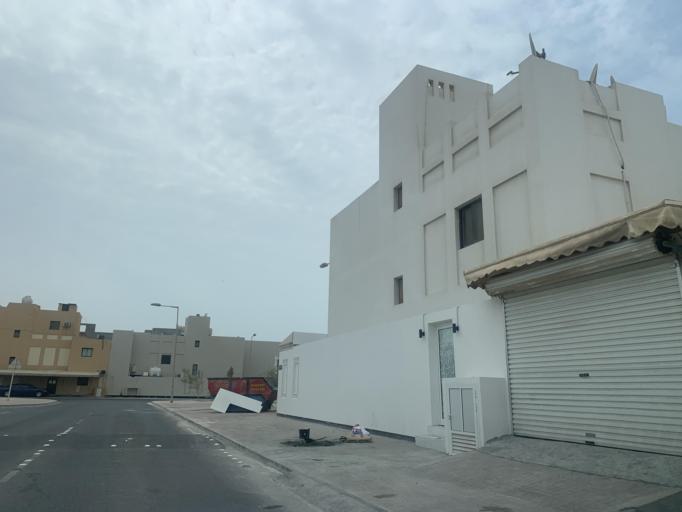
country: BH
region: Muharraq
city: Al Muharraq
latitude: 26.2827
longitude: 50.6404
